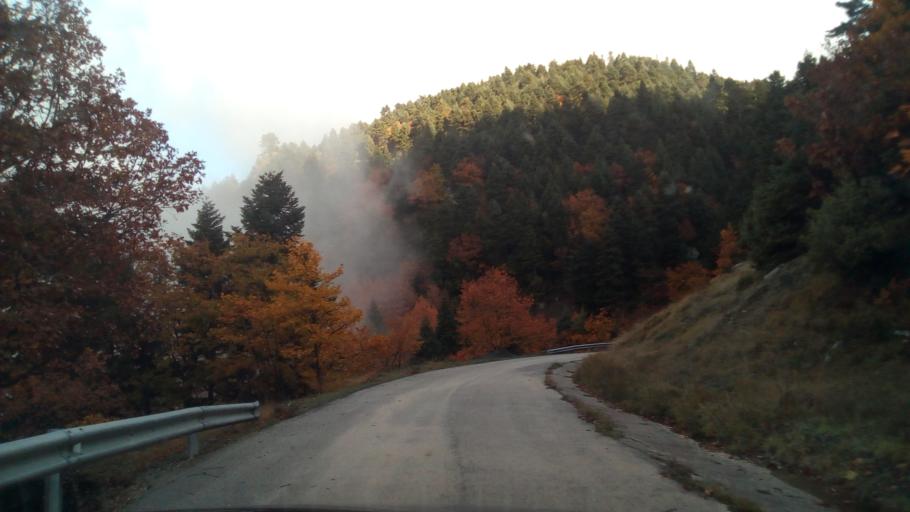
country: GR
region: West Greece
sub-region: Nomos Aitolias kai Akarnanias
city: Nafpaktos
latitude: 38.5611
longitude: 21.9287
